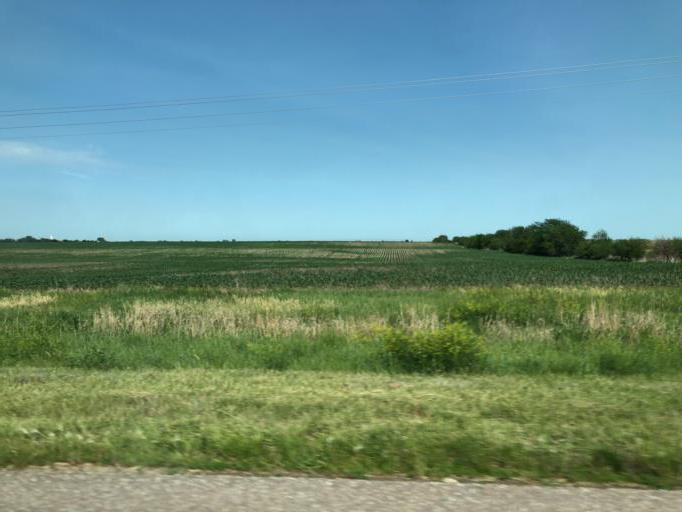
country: US
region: Nebraska
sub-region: Fillmore County
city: Geneva
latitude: 40.5750
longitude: -97.5956
